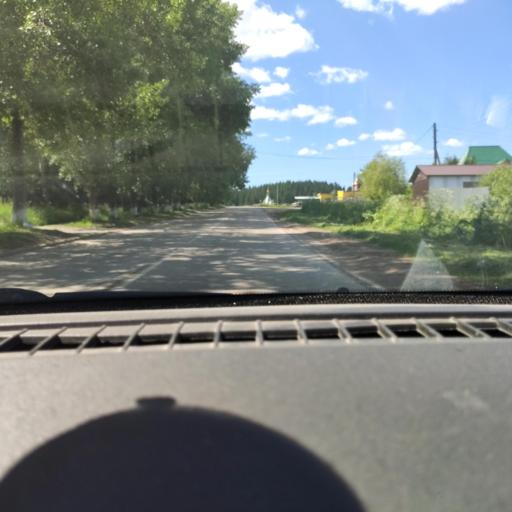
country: RU
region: Perm
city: Chaykovskaya
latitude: 58.1065
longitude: 55.5774
